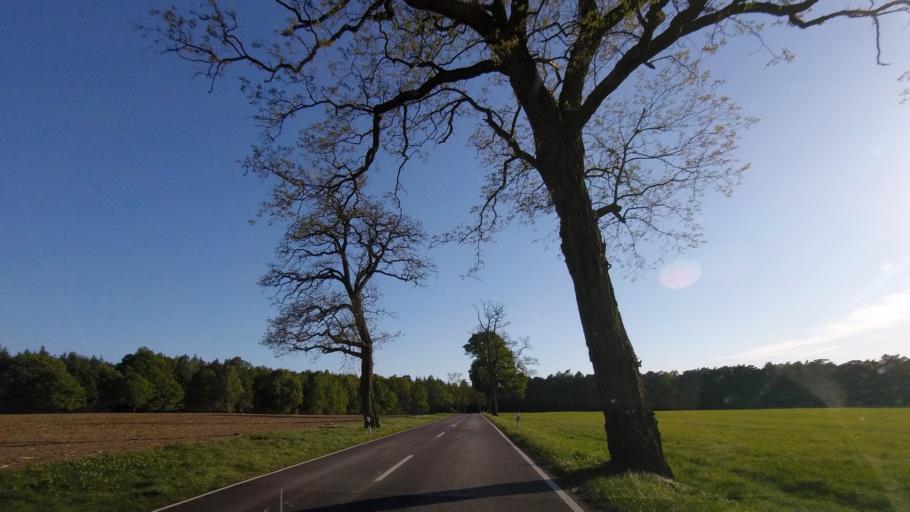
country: DE
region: Brandenburg
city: Baruth
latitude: 52.0086
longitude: 13.4450
